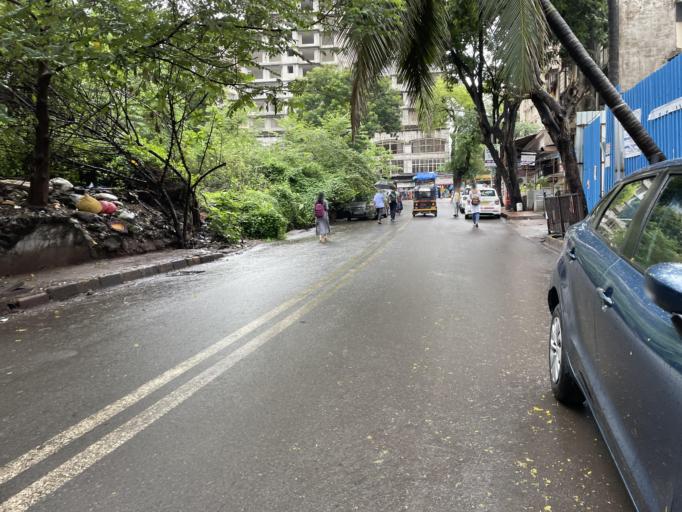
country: IN
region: Maharashtra
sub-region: Mumbai Suburban
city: Borivli
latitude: 19.2516
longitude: 72.8630
